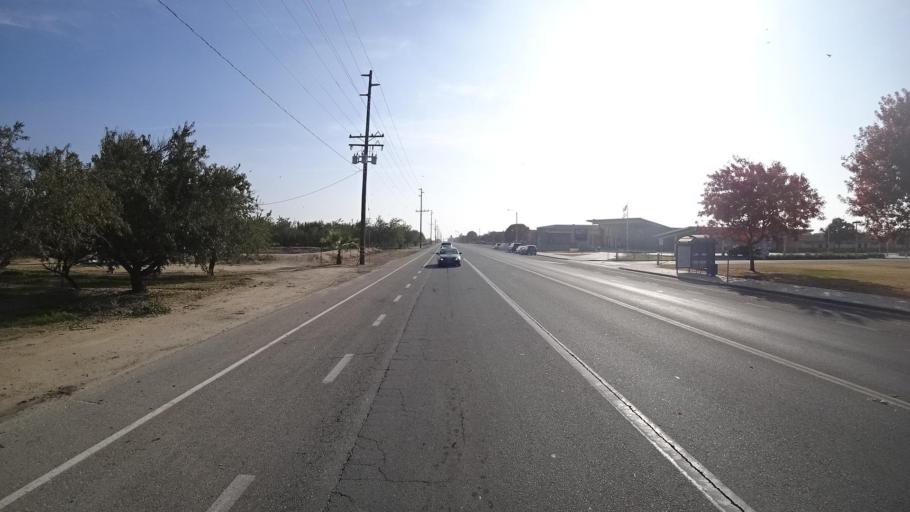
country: US
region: California
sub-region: Kern County
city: Delano
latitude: 35.7753
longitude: -119.2232
